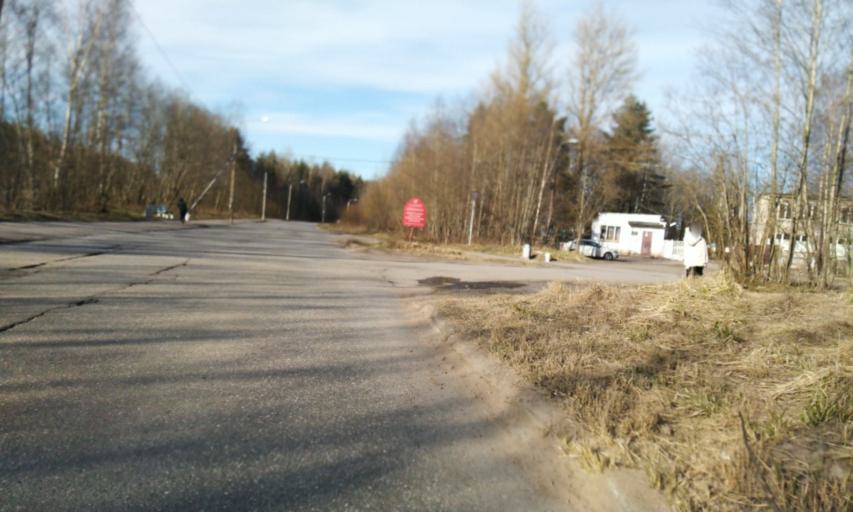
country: RU
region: Leningrad
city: Toksovo
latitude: 60.1150
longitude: 30.4871
